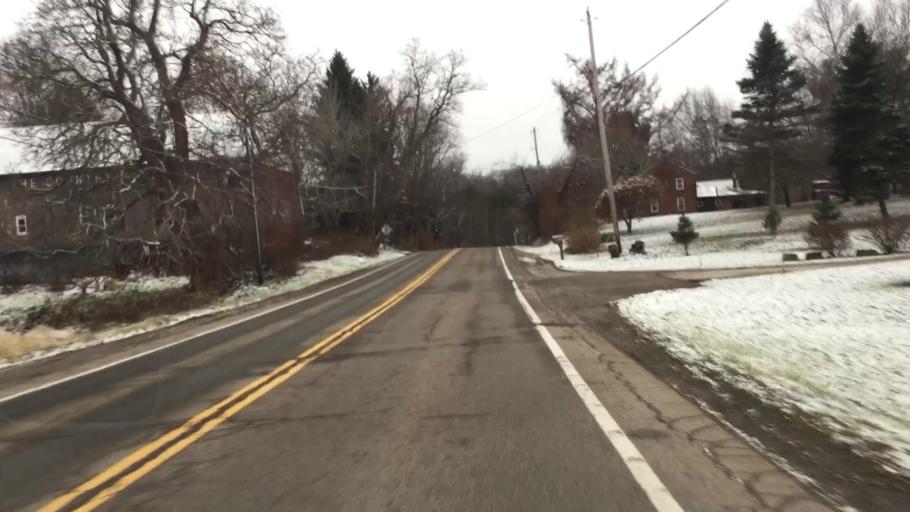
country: US
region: Ohio
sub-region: Summit County
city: Norton
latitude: 41.0740
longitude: -81.6391
